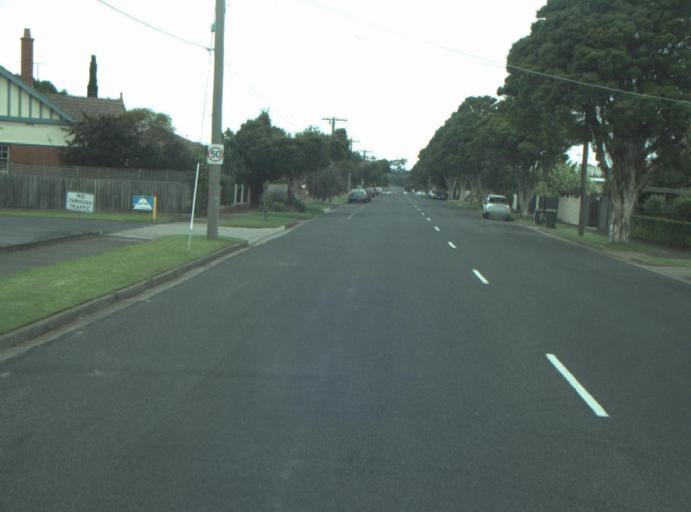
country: AU
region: Victoria
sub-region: Greater Geelong
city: East Geelong
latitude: -38.1643
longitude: 144.3729
